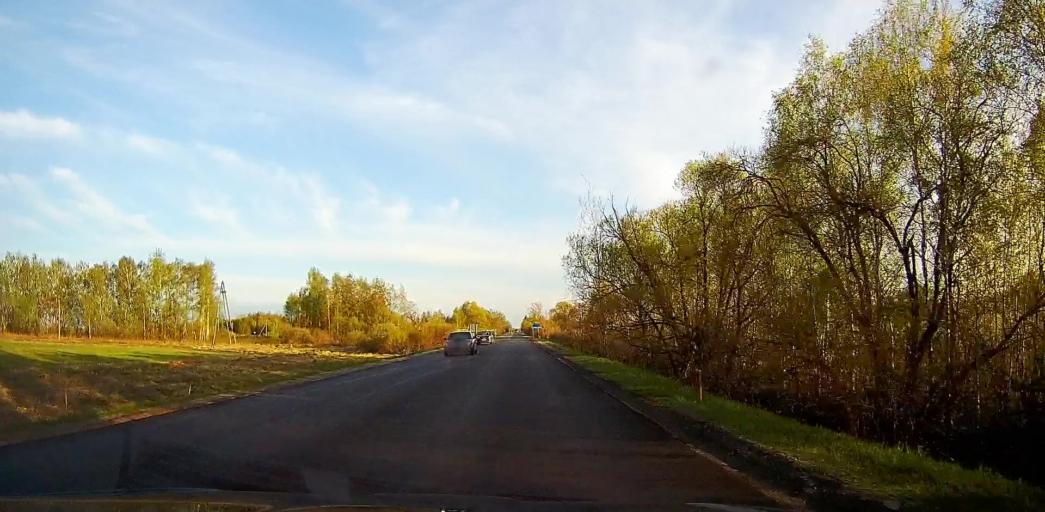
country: RU
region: Moskovskaya
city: Bronnitsy
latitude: 55.2797
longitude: 38.2184
